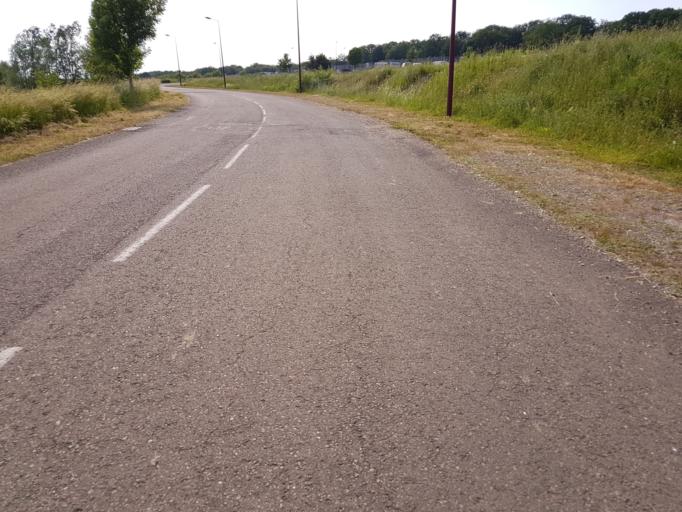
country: FR
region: Franche-Comte
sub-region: Departement de la Haute-Saone
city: Luxeuil-les-Bains
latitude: 47.8080
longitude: 6.3597
